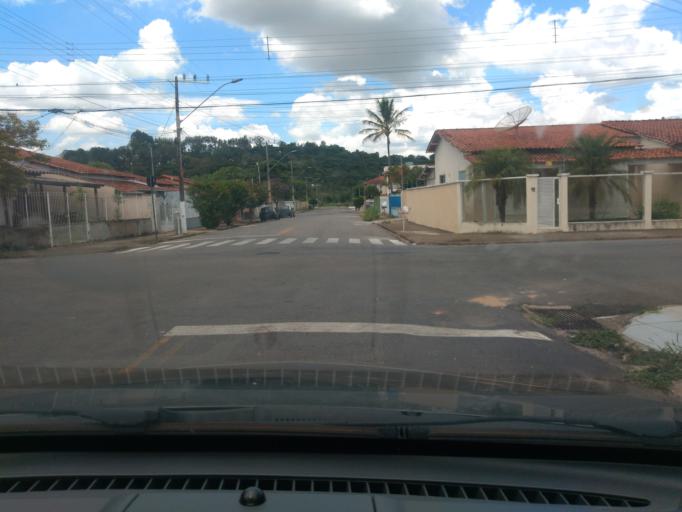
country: BR
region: Minas Gerais
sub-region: Tres Coracoes
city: Tres Coracoes
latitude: -21.6708
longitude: -45.2684
